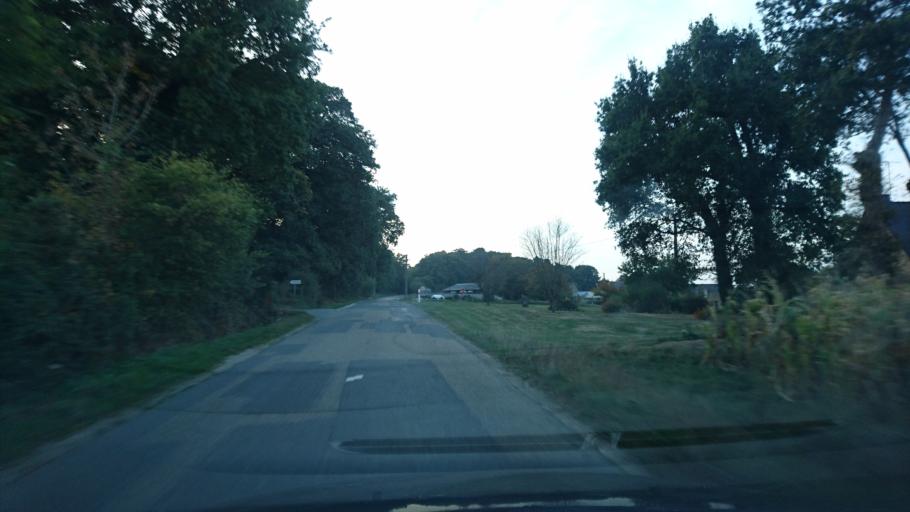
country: FR
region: Brittany
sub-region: Departement d'Ille-et-Vilaine
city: Maure-de-Bretagne
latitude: 47.8609
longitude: -2.0236
